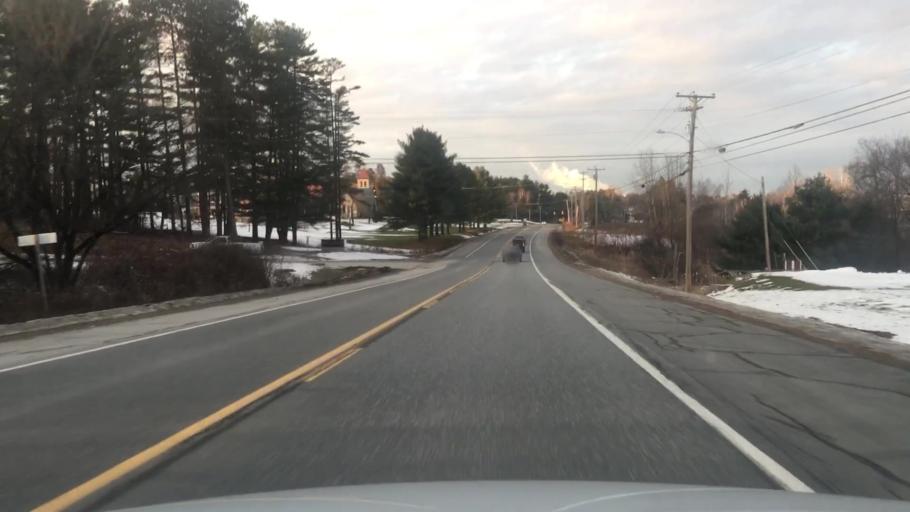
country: US
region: Maine
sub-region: Somerset County
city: Fairfield
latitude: 44.6666
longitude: -69.6285
